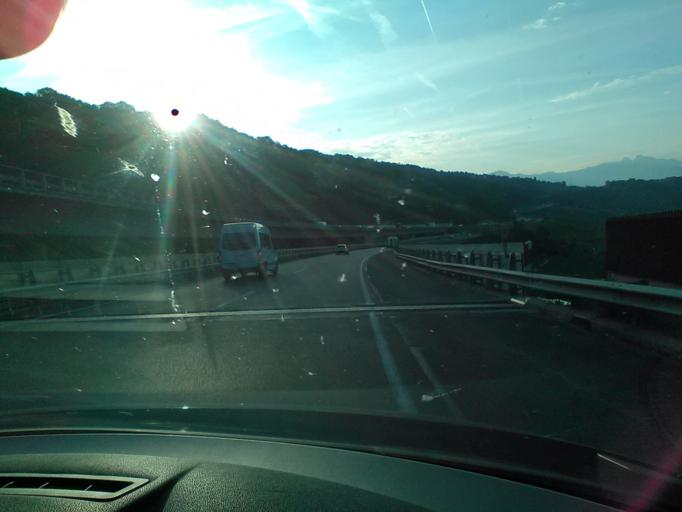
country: CH
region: Vaud
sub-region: Lavaux-Oron District
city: Cully
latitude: 46.4999
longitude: 6.7335
